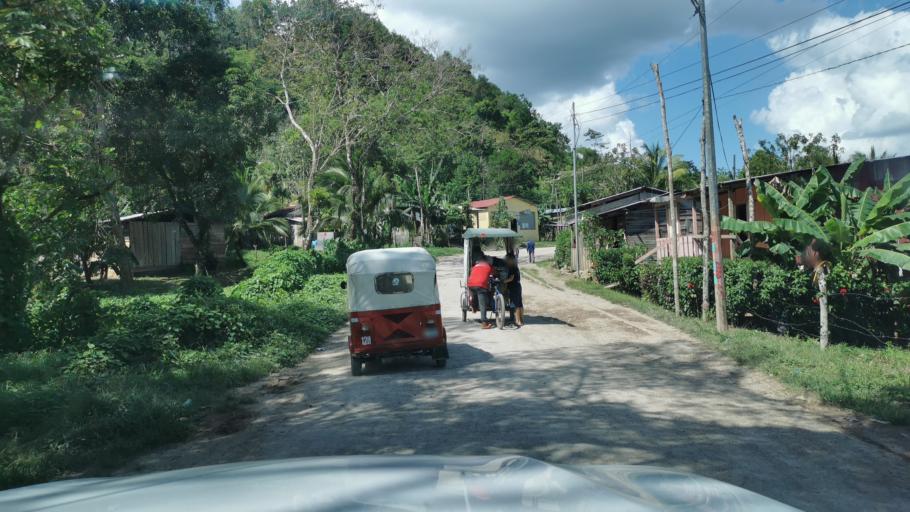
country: NI
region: Atlantico Sur
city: Rama
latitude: 12.1672
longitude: -84.2152
